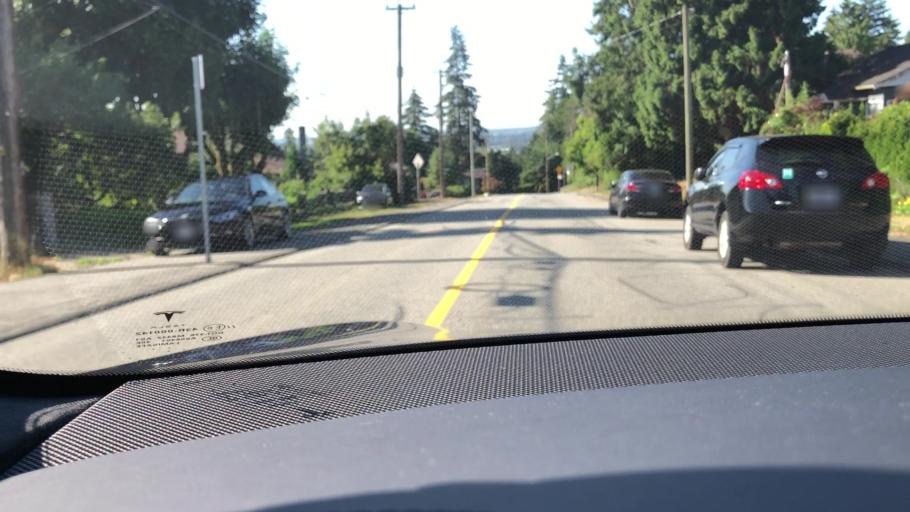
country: CA
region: British Columbia
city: Burnaby
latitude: 49.2128
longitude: -122.9719
